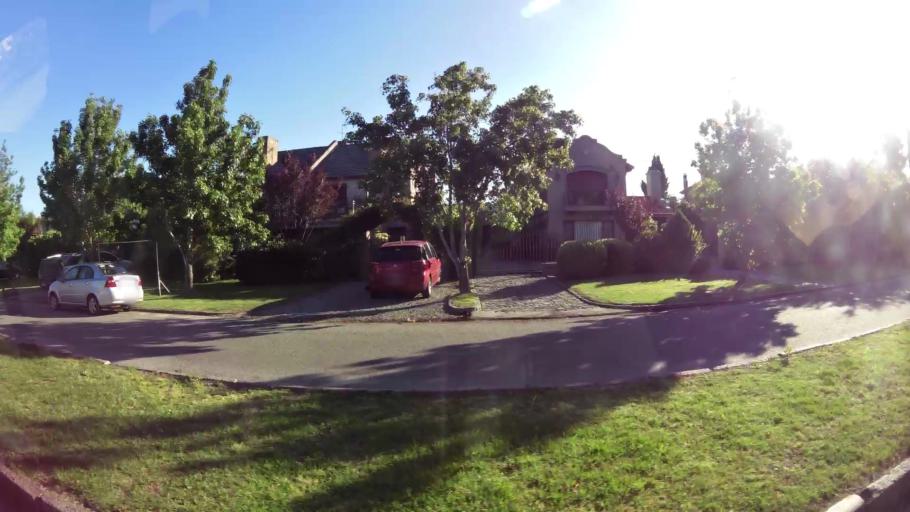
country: UY
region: Canelones
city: Paso de Carrasco
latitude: -34.8702
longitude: -56.0431
